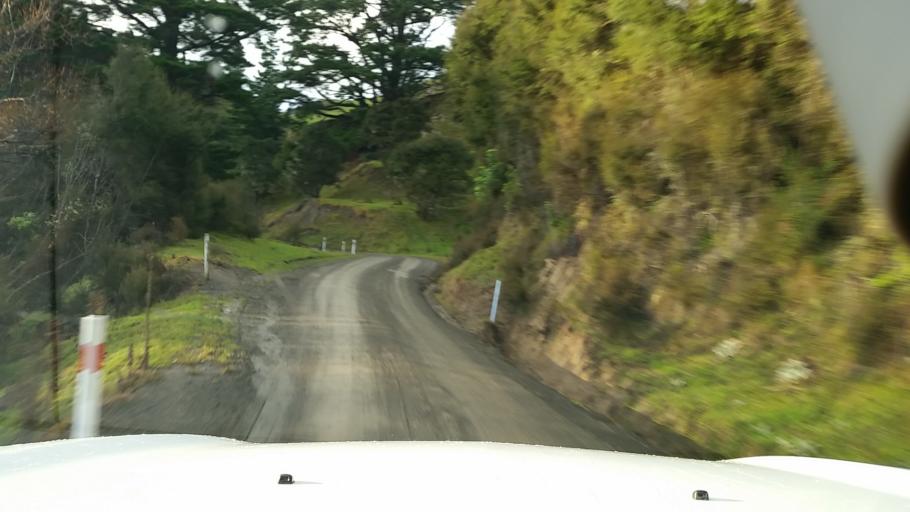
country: NZ
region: Wellington
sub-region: South Wairarapa District
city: Waipawa
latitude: -41.3248
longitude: 175.6572
